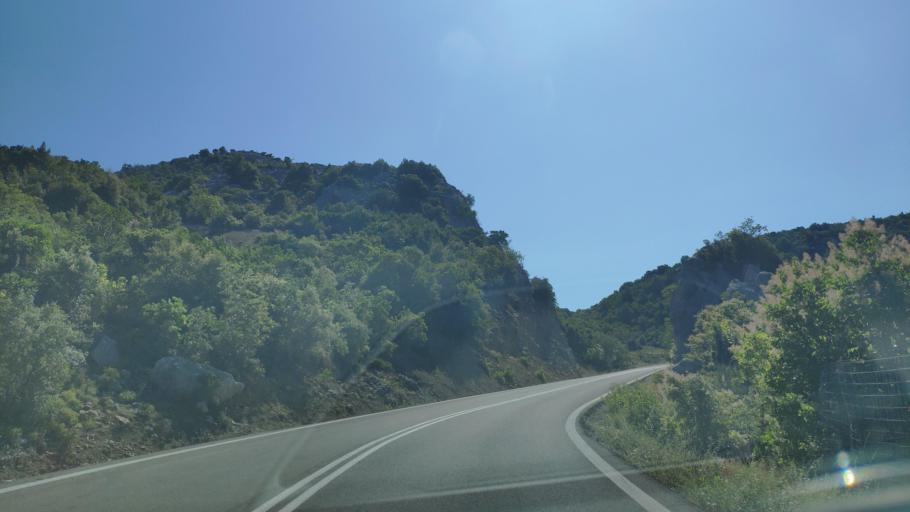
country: GR
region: West Greece
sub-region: Nomos Aitolias kai Akarnanias
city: Sardinia
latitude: 38.9251
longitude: 21.4178
